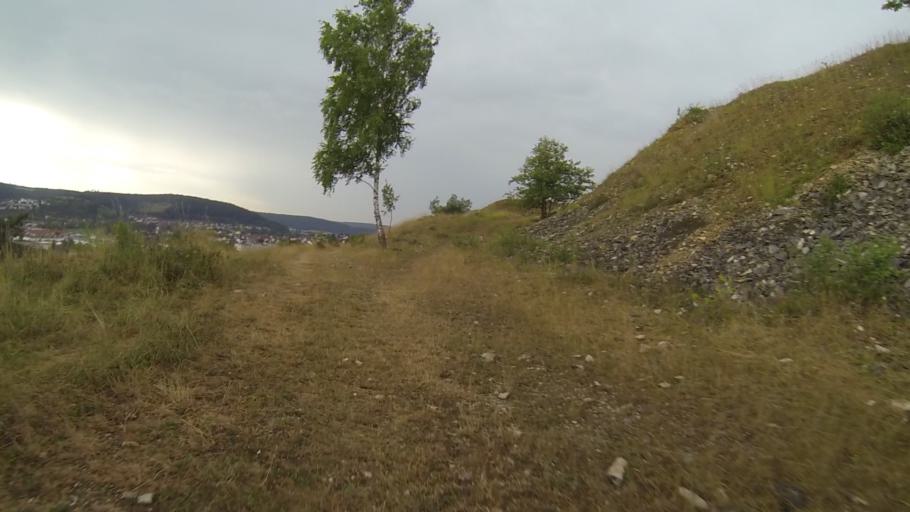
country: DE
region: Baden-Wuerttemberg
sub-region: Regierungsbezirk Stuttgart
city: Heidenheim an der Brenz
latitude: 48.7000
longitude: 10.1753
